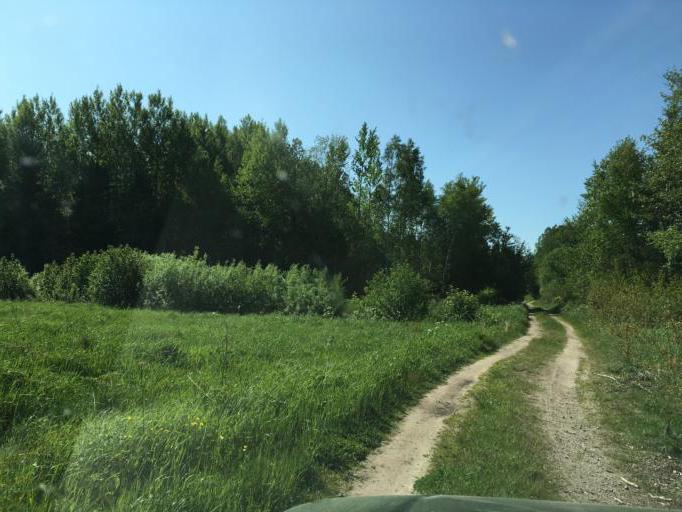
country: LV
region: Ventspils
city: Ventspils
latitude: 57.4798
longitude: 21.7631
